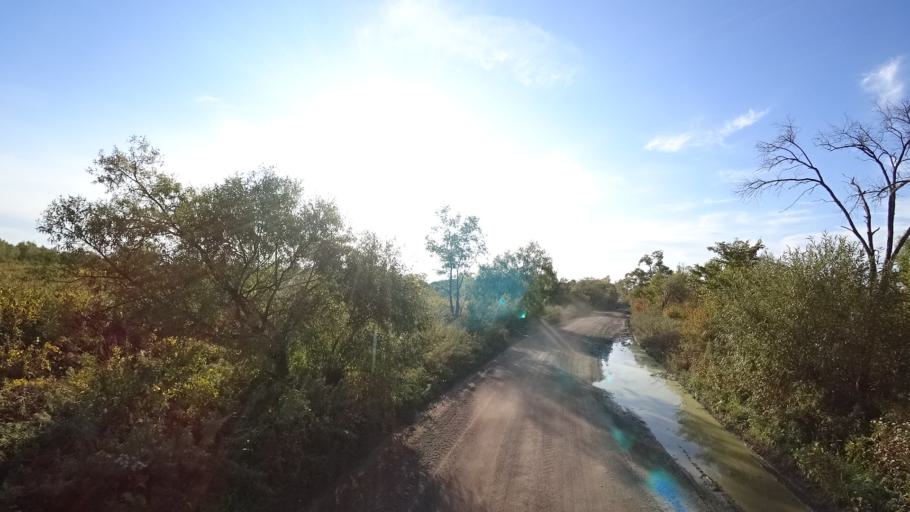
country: RU
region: Amur
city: Arkhara
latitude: 49.3558
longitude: 130.1294
